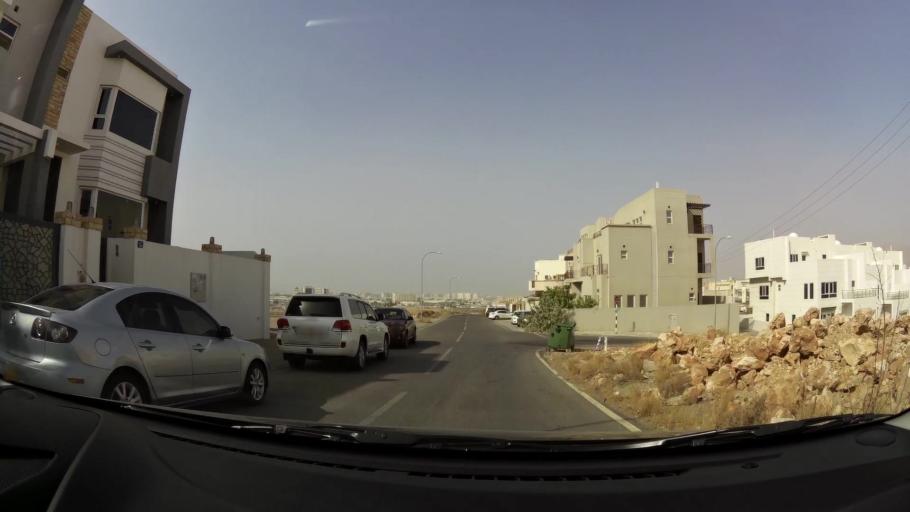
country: OM
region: Muhafazat Masqat
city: Bawshar
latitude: 23.5599
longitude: 58.3499
